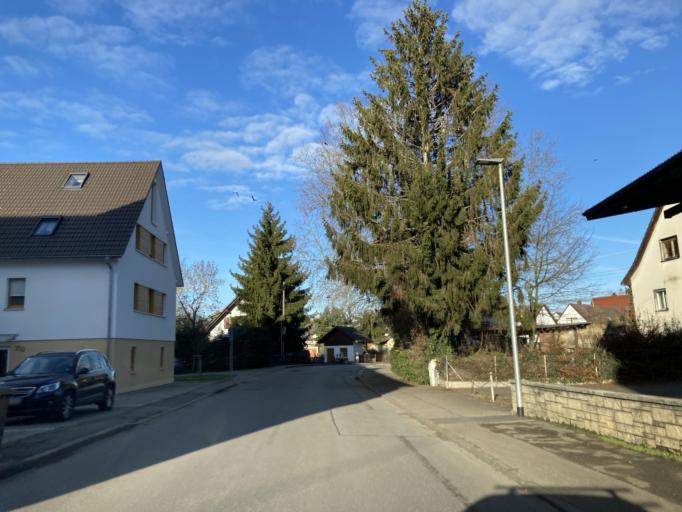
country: DE
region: Baden-Wuerttemberg
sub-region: Freiburg Region
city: Unterkrozingen
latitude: 47.9393
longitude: 7.6887
